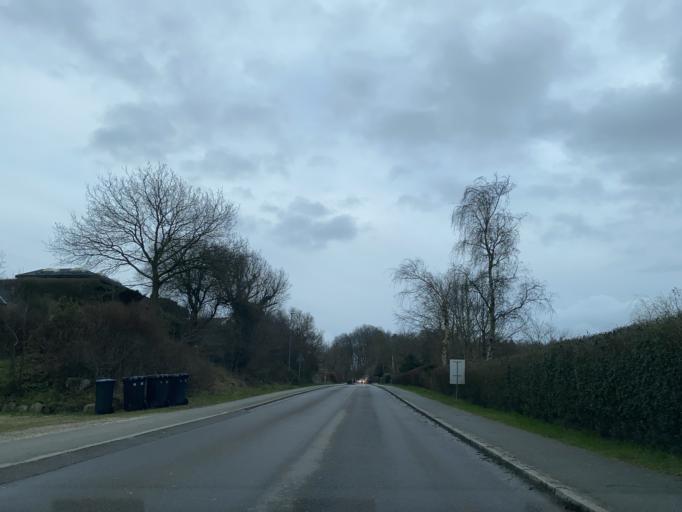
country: DK
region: Central Jutland
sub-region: Viborg Kommune
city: Bjerringbro
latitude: 56.3048
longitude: 9.5952
